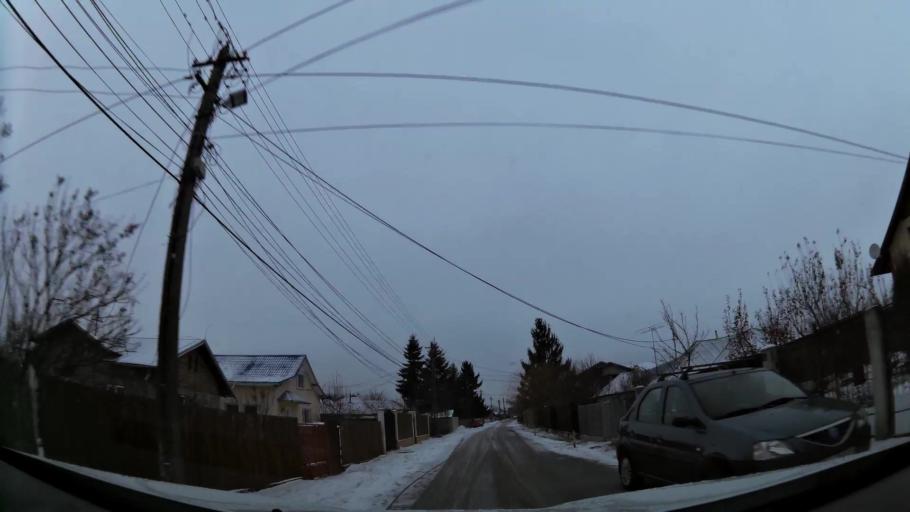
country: RO
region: Prahova
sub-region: Comuna Berceni
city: Corlatesti
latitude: 44.9124
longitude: 26.0920
